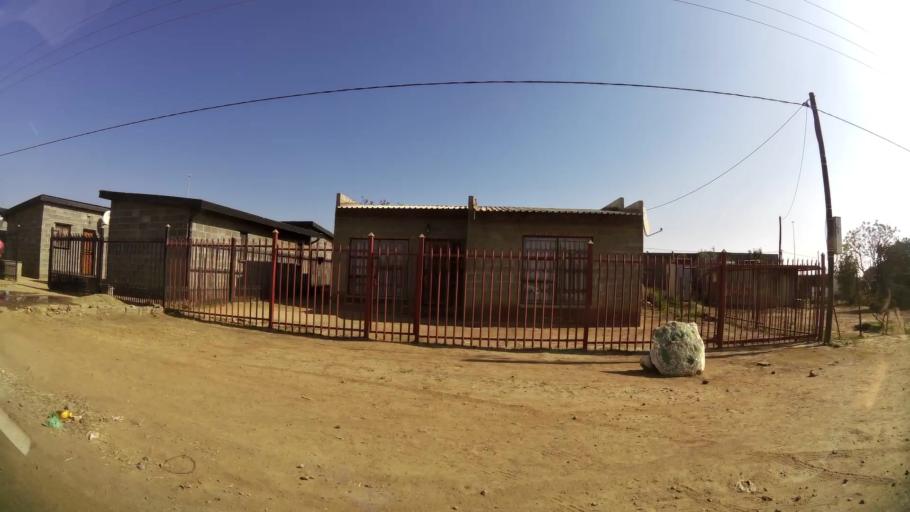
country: ZA
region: Orange Free State
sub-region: Mangaung Metropolitan Municipality
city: Bloemfontein
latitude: -29.1781
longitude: 26.2884
